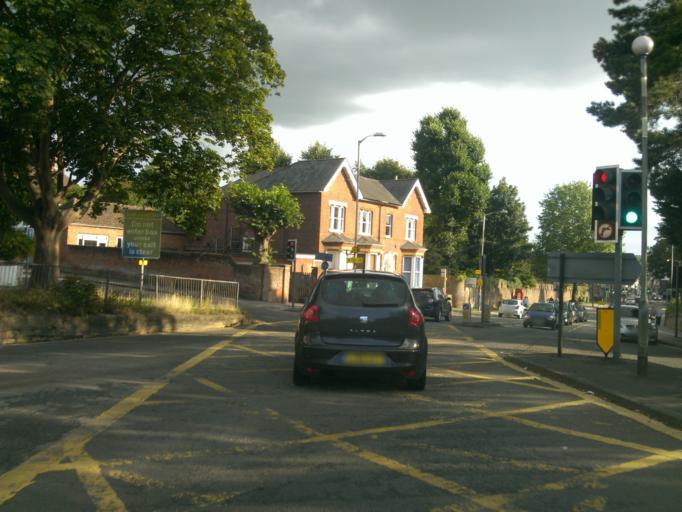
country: GB
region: England
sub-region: Kent
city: Tonbridge
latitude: 51.2011
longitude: 0.2768
